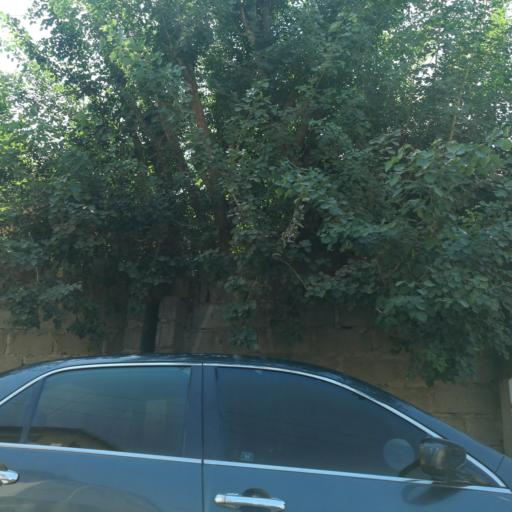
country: NG
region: Kano
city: Kano
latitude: 12.0038
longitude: 8.5406
